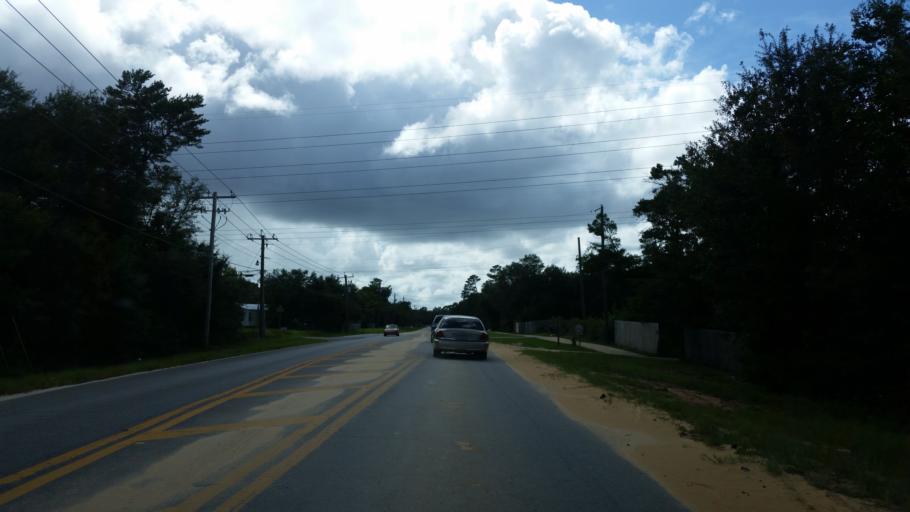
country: US
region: Florida
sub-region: Santa Rosa County
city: Holley
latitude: 30.4461
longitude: -86.9365
